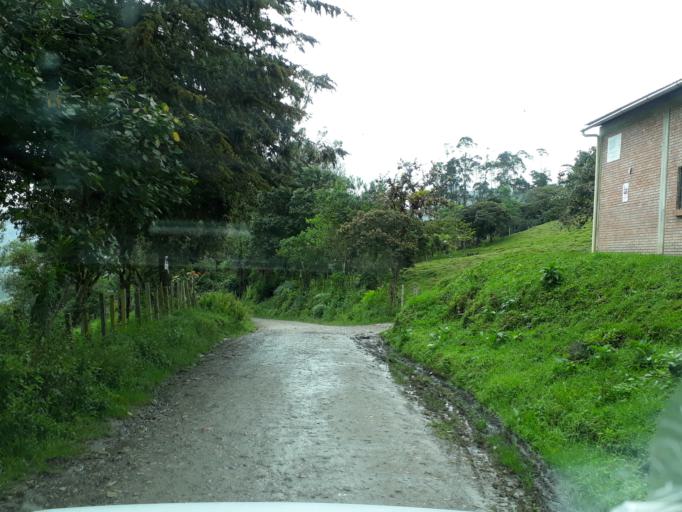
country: CO
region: Cundinamarca
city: Gacheta
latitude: 4.8575
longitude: -73.6408
